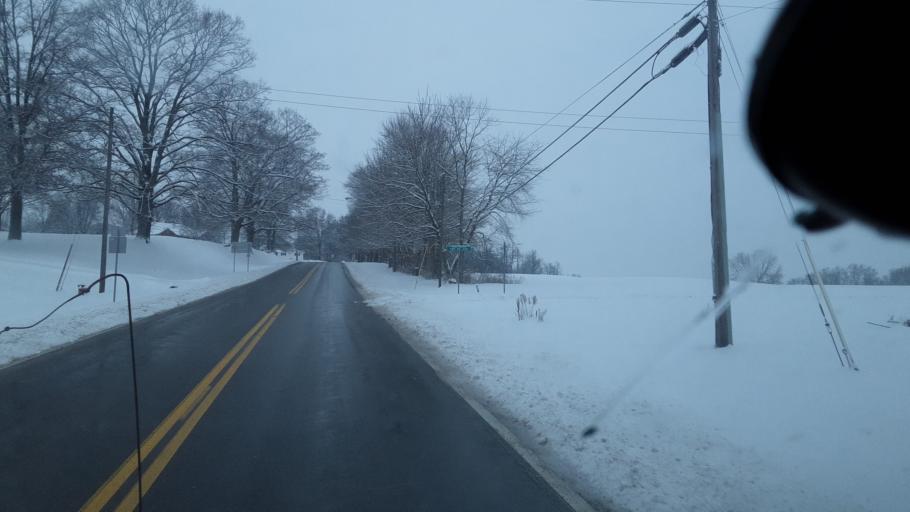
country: US
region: Ohio
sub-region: Perry County
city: Thornport
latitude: 39.8983
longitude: -82.4103
